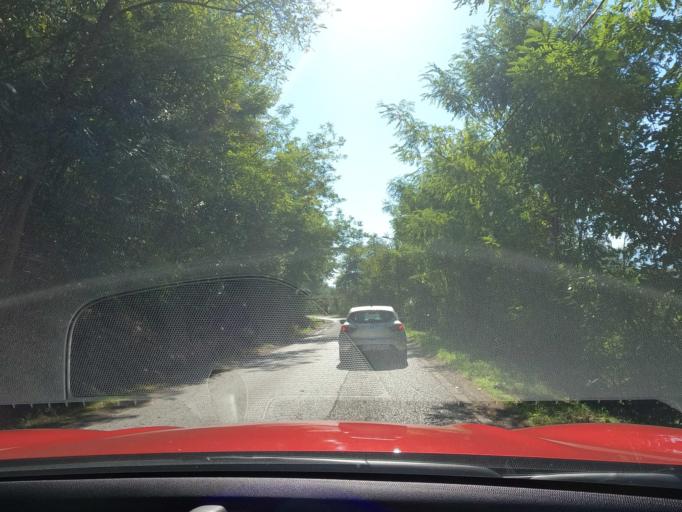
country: RS
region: Central Serbia
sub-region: Raski Okrug
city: Kraljevo
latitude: 43.7367
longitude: 20.7397
